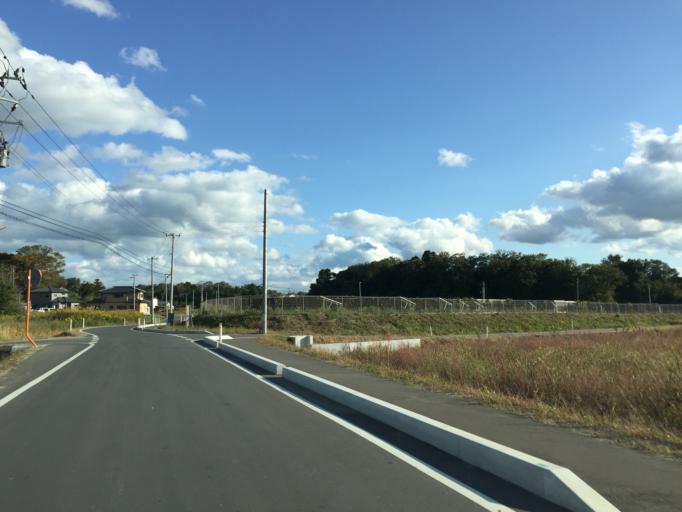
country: JP
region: Miyagi
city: Marumori
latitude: 37.8706
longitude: 140.9303
